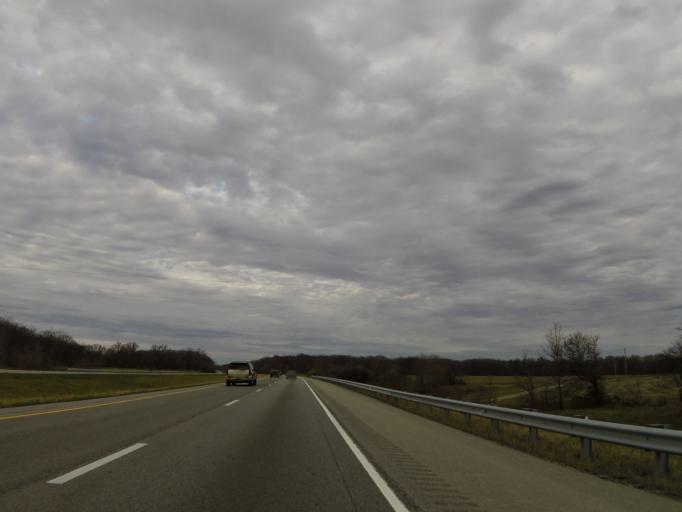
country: US
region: Illinois
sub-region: Clinton County
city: Wamac
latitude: 38.3757
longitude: -89.1028
